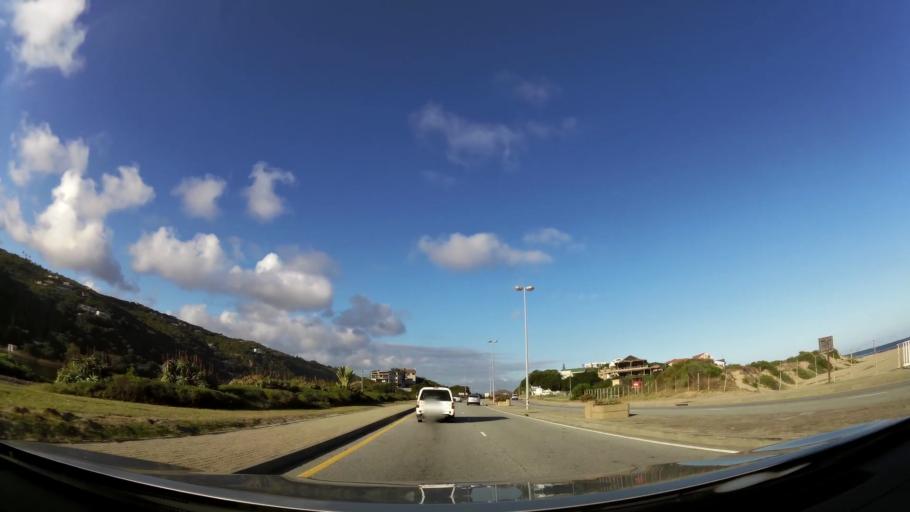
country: ZA
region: Western Cape
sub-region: Eden District Municipality
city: George
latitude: -33.9949
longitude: 22.5813
